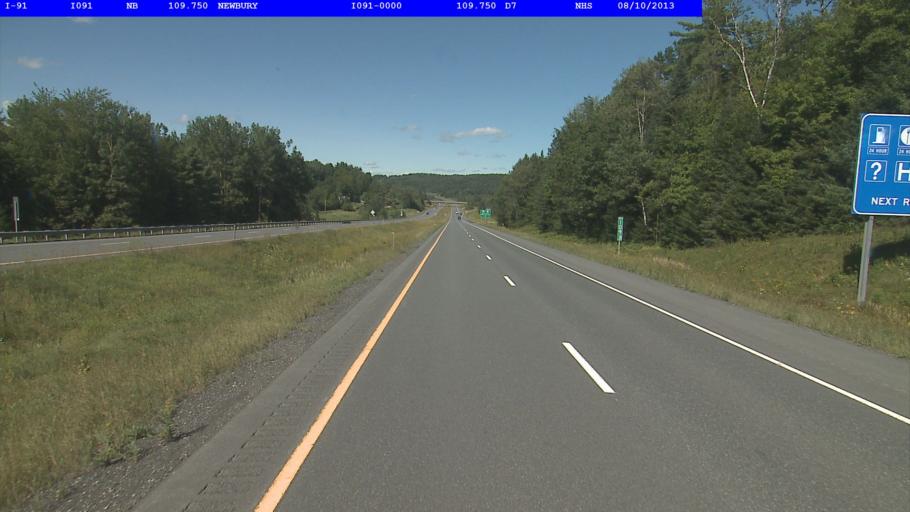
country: US
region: New Hampshire
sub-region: Grafton County
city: Woodsville
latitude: 44.1528
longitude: -72.0947
